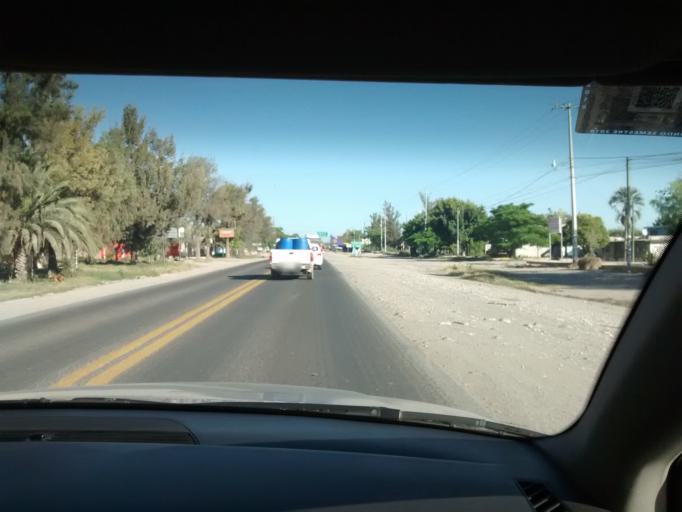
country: MX
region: Puebla
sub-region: Tehuacan
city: Magdalena Cuayucatepec
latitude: 18.5144
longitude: -97.4974
